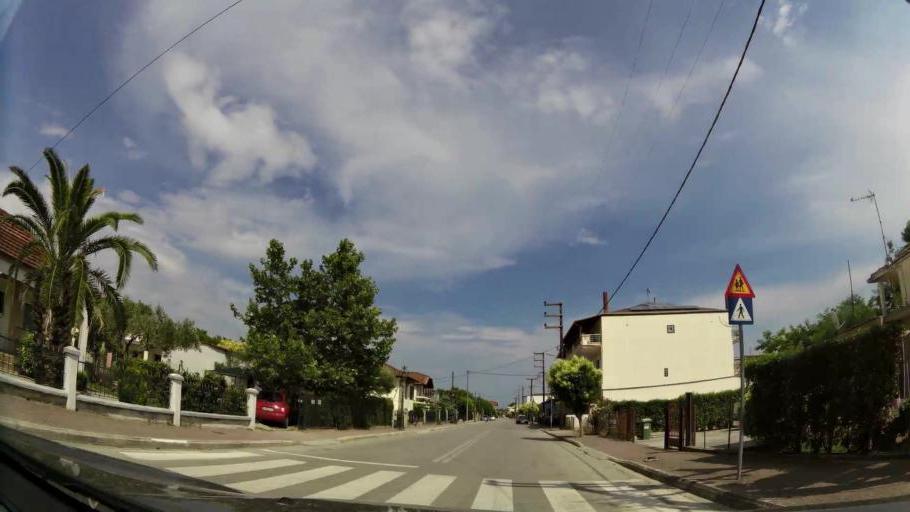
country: GR
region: Central Macedonia
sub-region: Nomos Pierias
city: Korinos
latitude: 40.3146
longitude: 22.5891
